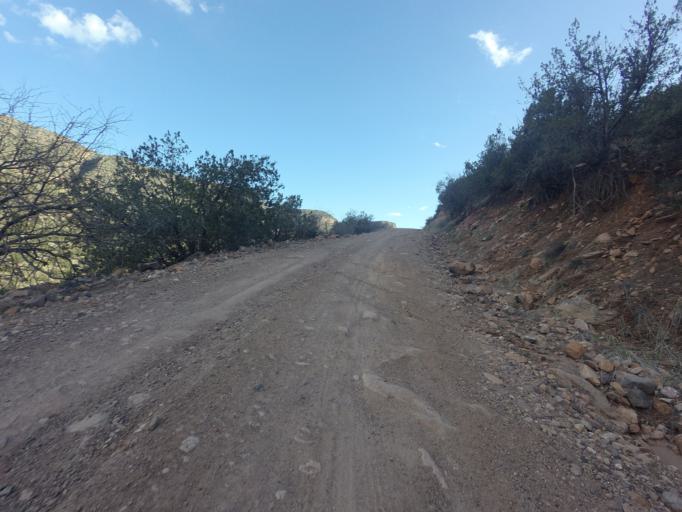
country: US
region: Arizona
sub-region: Gila County
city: Pine
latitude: 34.3778
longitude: -111.6602
